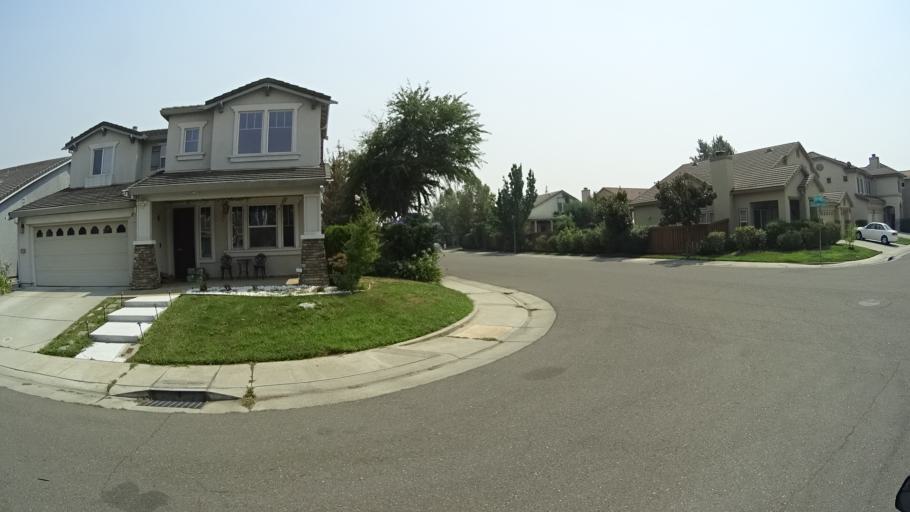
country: US
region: California
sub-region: Sacramento County
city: Laguna
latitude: 38.4041
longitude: -121.4309
